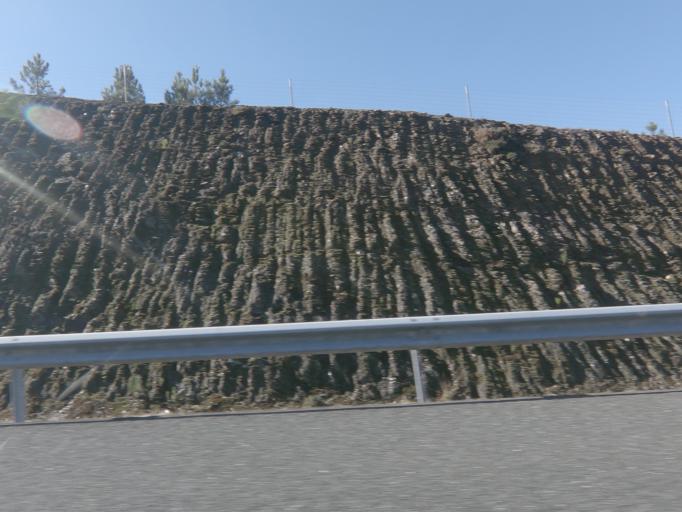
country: ES
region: Galicia
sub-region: Provincia de Pontevedra
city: Lalin
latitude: 42.6038
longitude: -8.0988
